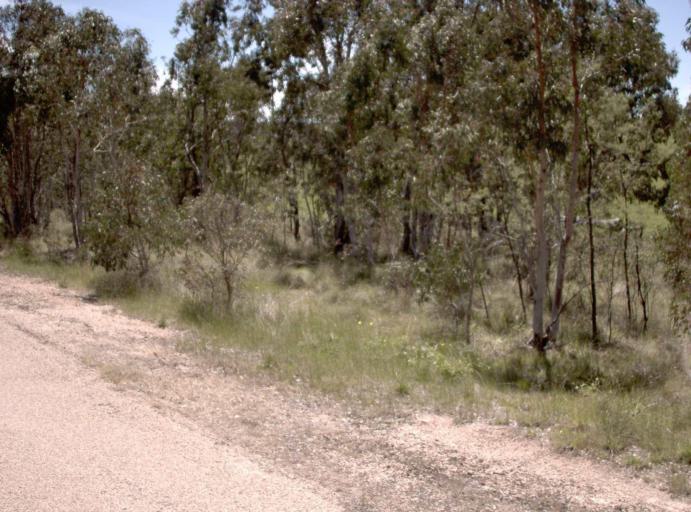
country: AU
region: New South Wales
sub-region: Snowy River
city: Jindabyne
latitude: -37.0560
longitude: 148.2593
